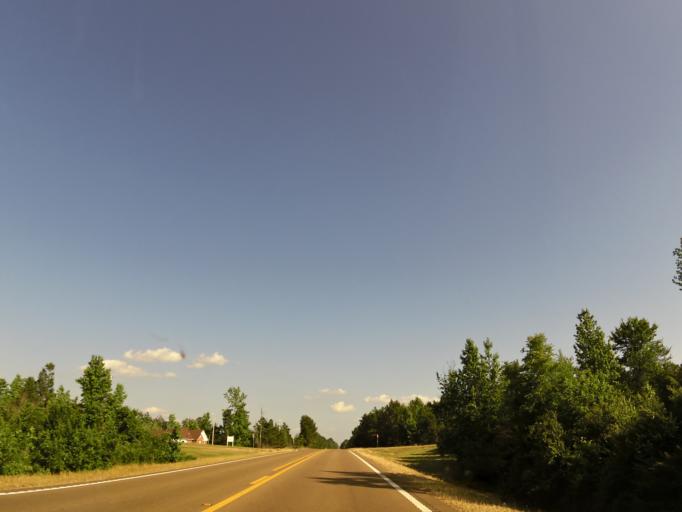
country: US
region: Mississippi
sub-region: Lafayette County
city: University
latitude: 34.2446
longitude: -89.5112
